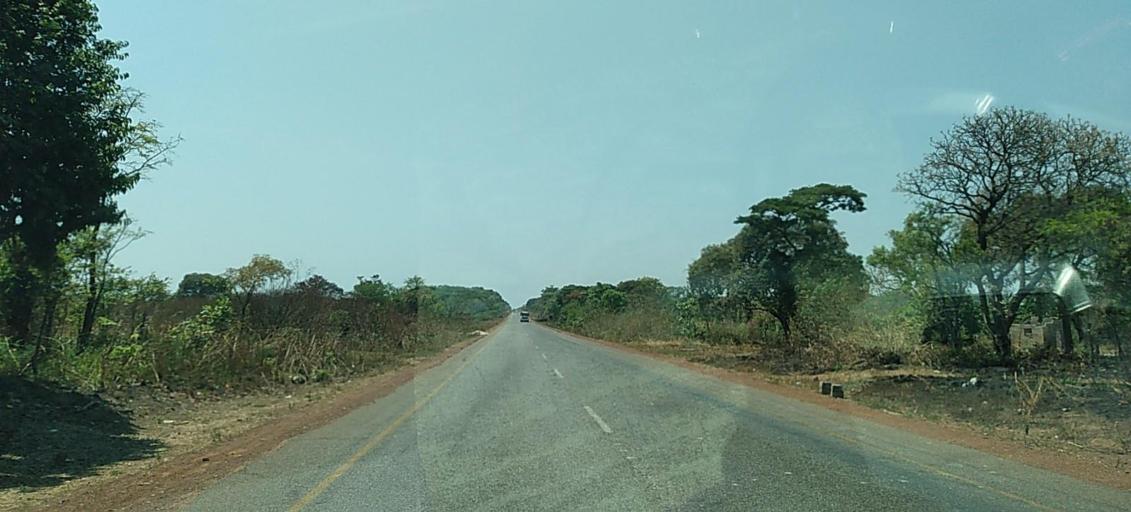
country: ZM
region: North-Western
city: Solwezi
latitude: -12.3820
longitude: 26.1939
